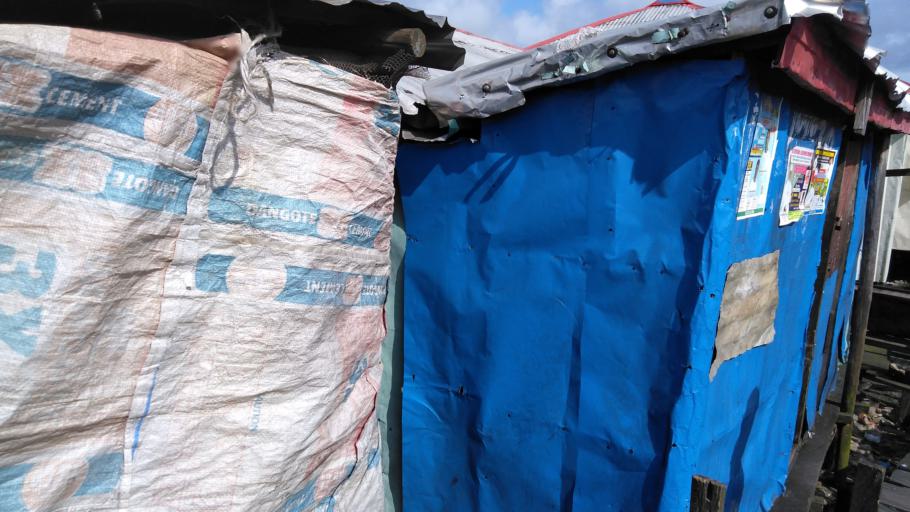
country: NG
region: Ondo
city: Igbekebo
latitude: 5.9212
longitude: 4.9668
